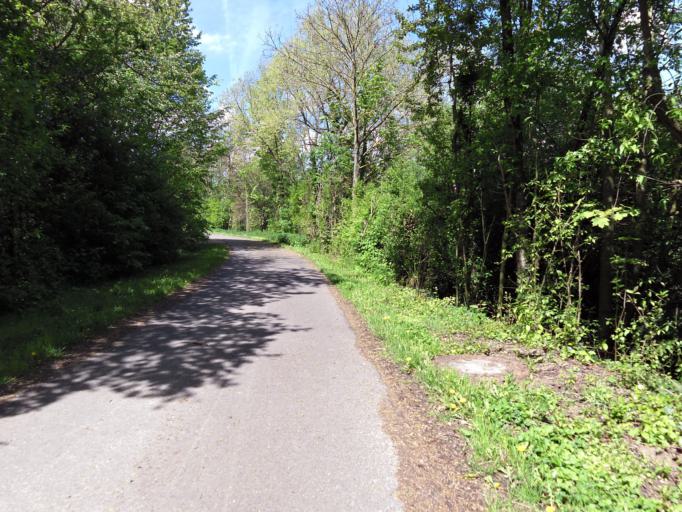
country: DE
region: Rheinland-Pfalz
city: Hangen-Weisheim
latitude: 49.7033
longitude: 8.1772
